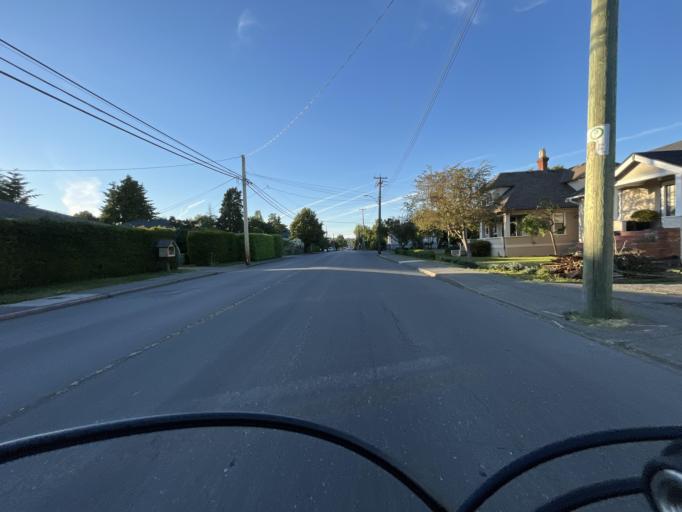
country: CA
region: British Columbia
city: Oak Bay
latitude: 48.4286
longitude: -123.3226
